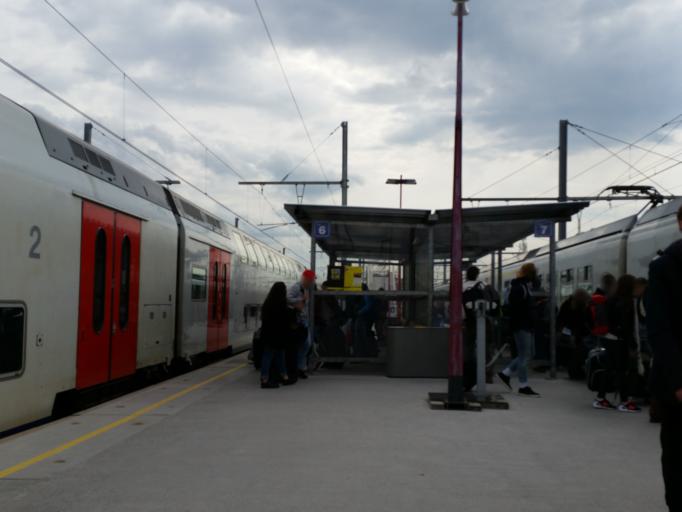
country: BE
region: Wallonia
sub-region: Province du Hainaut
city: Mons
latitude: 50.4551
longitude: 3.9426
